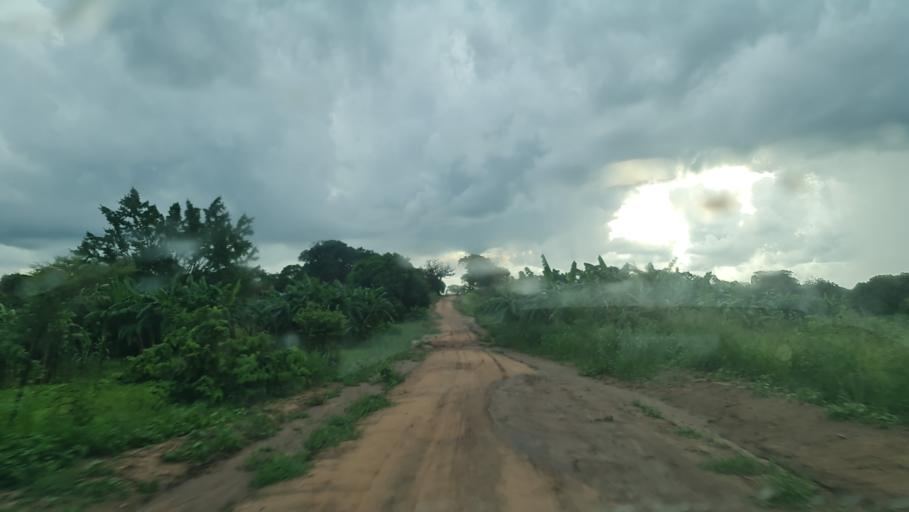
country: MZ
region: Nampula
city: Nacala
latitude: -13.9852
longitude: 40.3888
